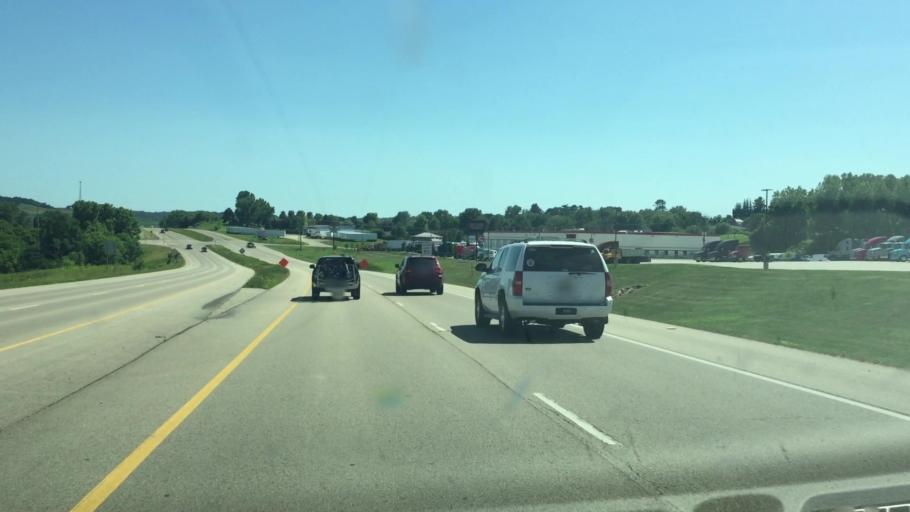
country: US
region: Iowa
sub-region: Dubuque County
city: Dubuque
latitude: 42.4513
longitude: -90.6797
